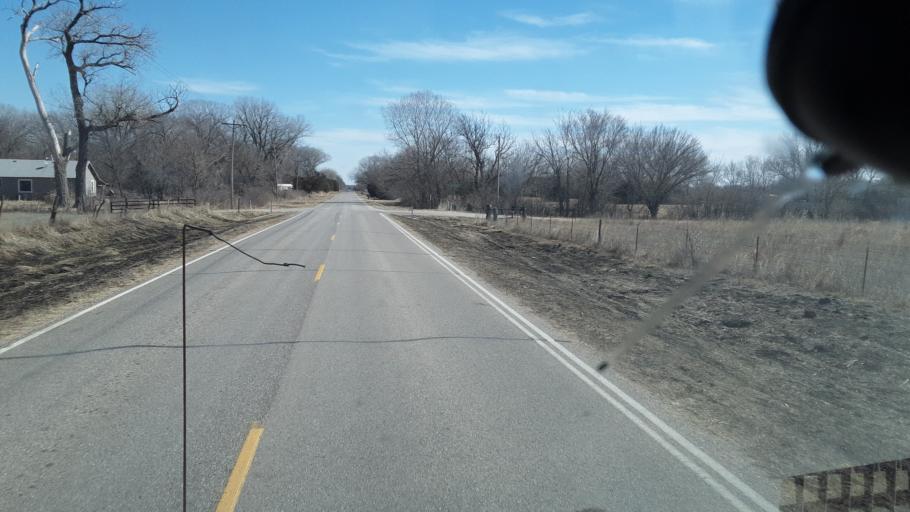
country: US
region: Kansas
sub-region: Reno County
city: Hutchinson
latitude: 38.1593
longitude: -97.8863
